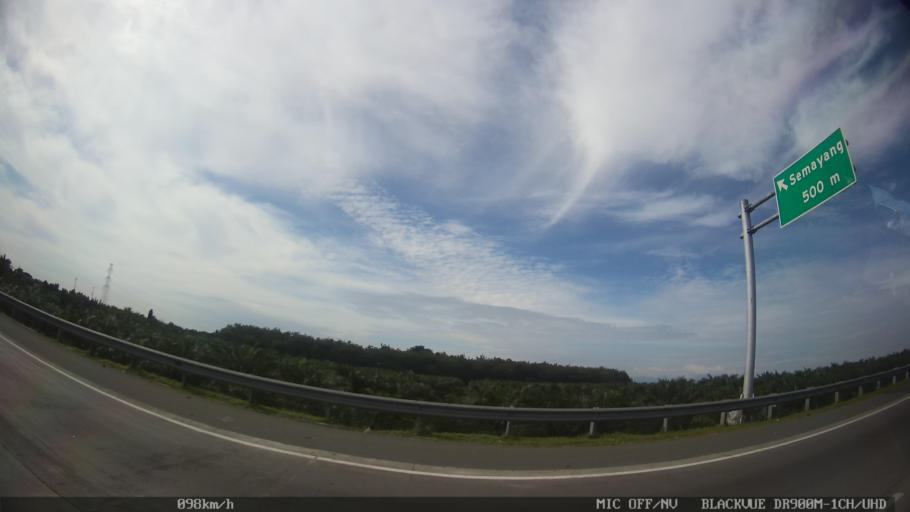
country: ID
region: North Sumatra
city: Sunggal
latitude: 3.6372
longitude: 98.5898
